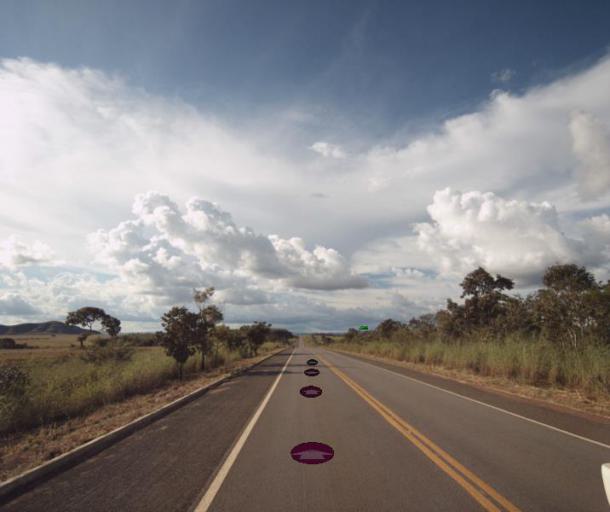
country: BR
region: Goias
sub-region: Barro Alto
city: Barro Alto
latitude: -14.8362
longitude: -48.6382
